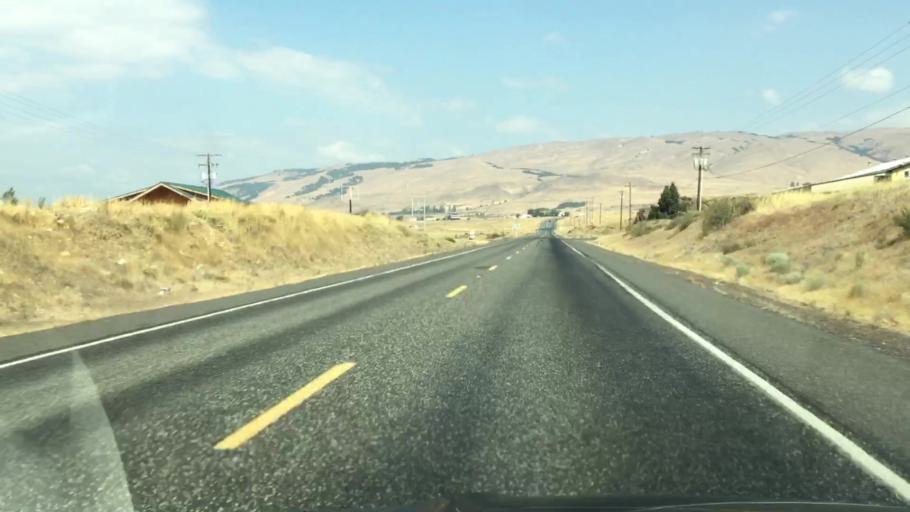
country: US
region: Washington
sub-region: Klickitat County
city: Dallesport
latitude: 45.6261
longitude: -121.1487
